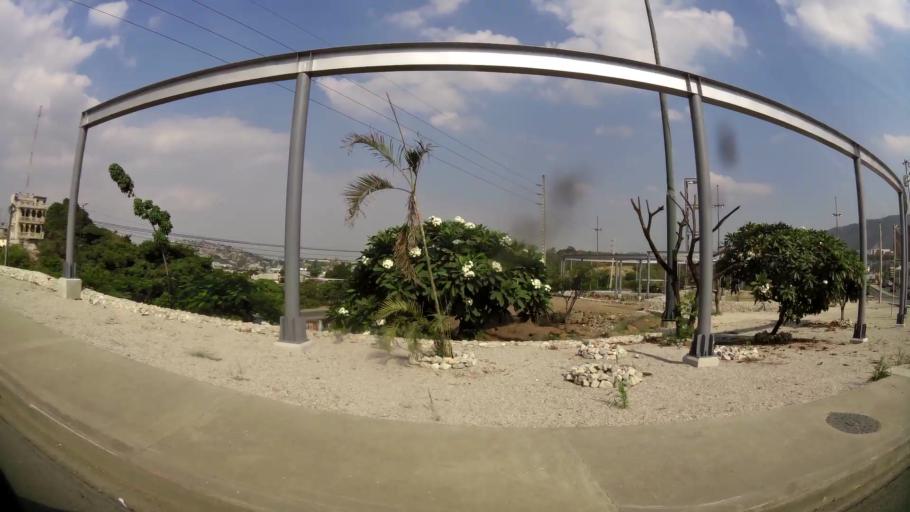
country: EC
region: Guayas
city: Santa Lucia
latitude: -2.1404
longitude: -79.9464
